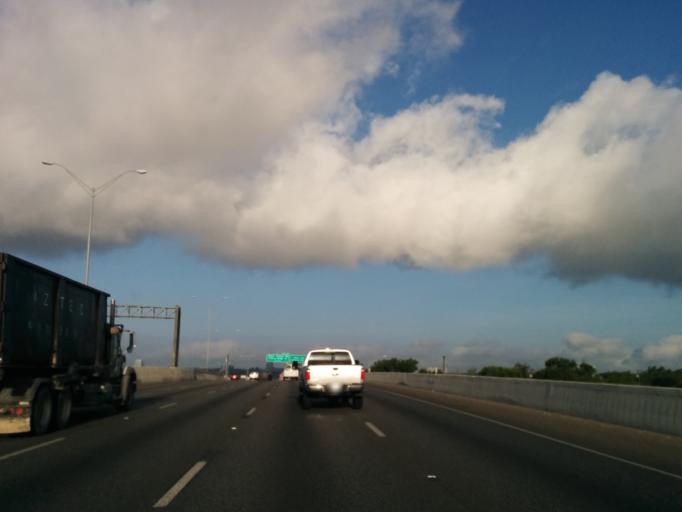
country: US
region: Texas
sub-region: Bexar County
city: Castle Hills
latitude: 29.5201
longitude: -98.5182
